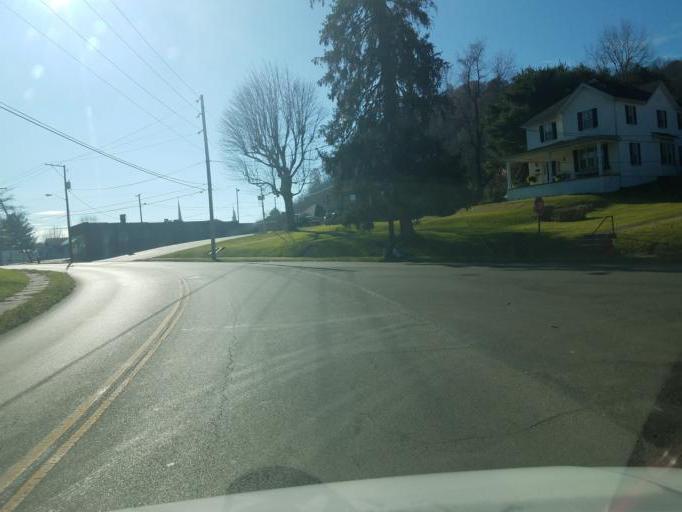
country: US
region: Ohio
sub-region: Scioto County
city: Sciotodale
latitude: 38.7620
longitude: -82.8932
